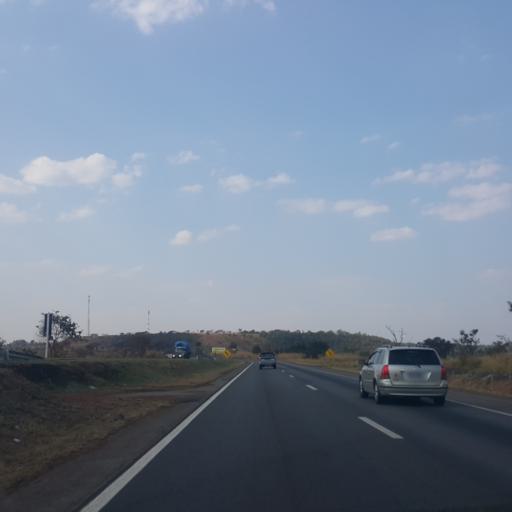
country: BR
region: Goias
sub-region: Abadiania
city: Abadiania
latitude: -16.1091
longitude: -48.5271
